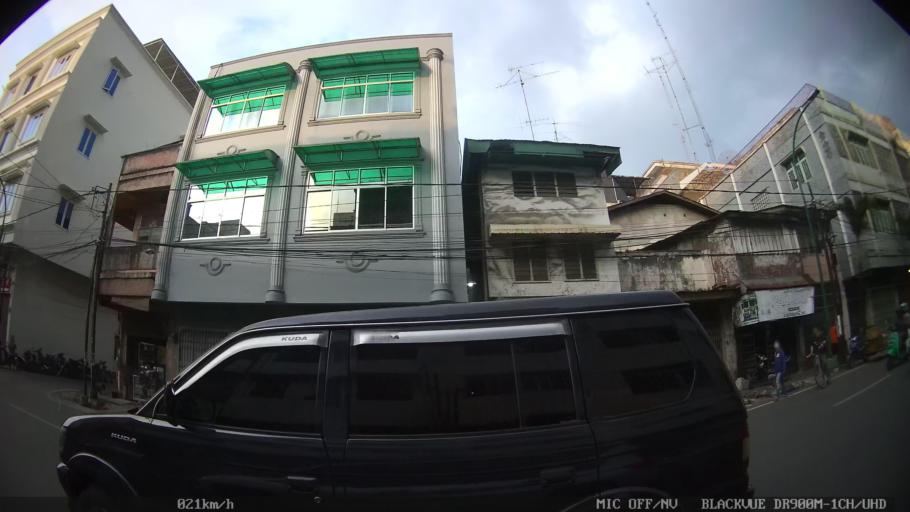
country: ID
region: North Sumatra
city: Medan
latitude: 3.5839
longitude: 98.6868
